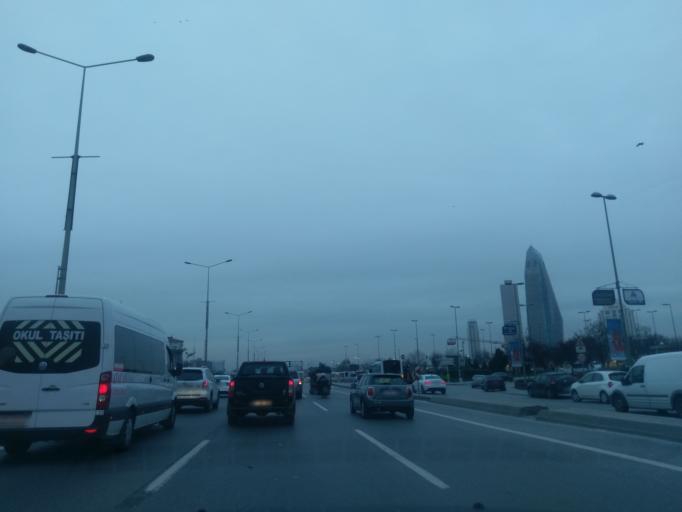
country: TR
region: Istanbul
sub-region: Atasehir
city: Atasehir
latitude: 40.9741
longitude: 29.0998
